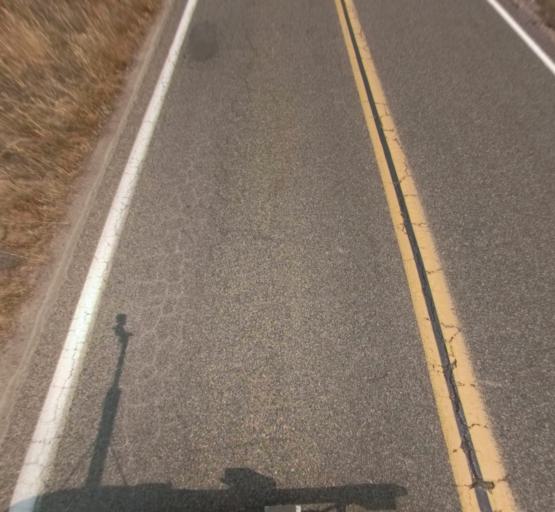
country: US
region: California
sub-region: Madera County
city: Yosemite Lakes
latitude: 37.1936
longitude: -119.9091
